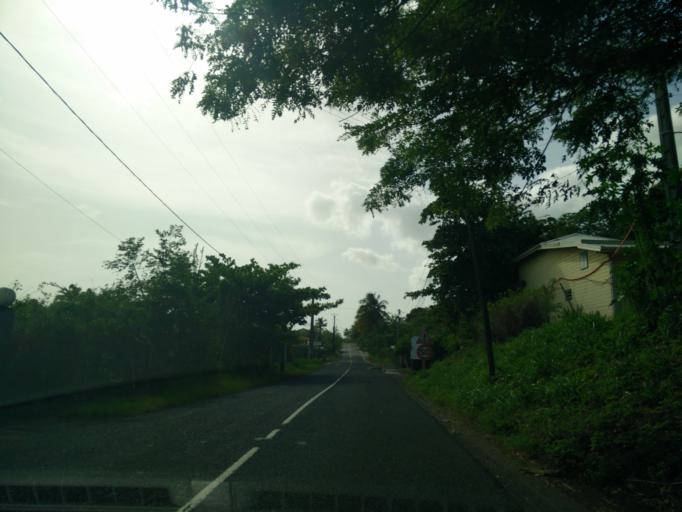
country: MQ
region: Martinique
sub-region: Martinique
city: Saint-Pierre
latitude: 14.7587
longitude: -61.1860
